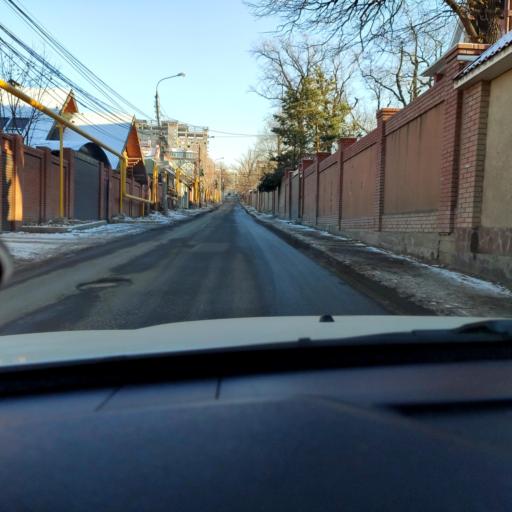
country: RU
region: Samara
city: Samara
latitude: 53.2604
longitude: 50.1988
